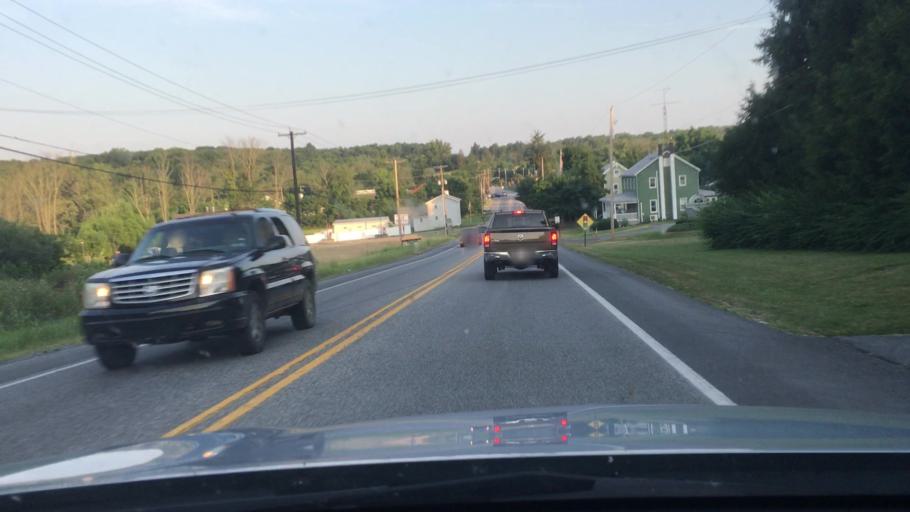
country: US
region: Pennsylvania
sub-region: York County
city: Dover
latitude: 40.0668
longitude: -76.9203
